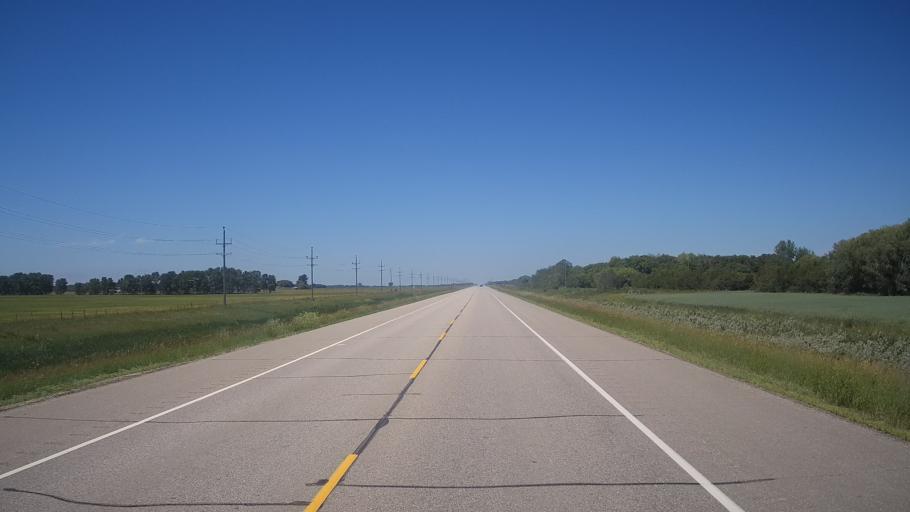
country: CA
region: Manitoba
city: Neepawa
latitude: 50.2257
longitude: -99.0488
